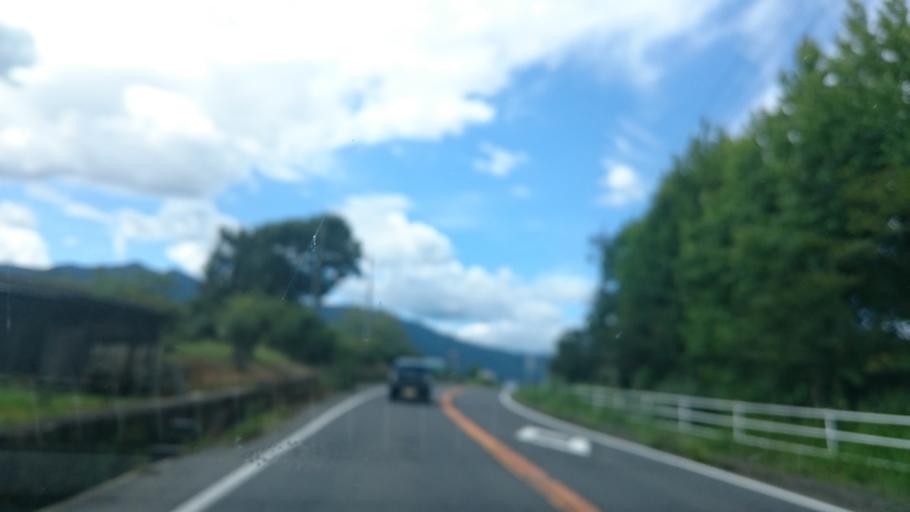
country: JP
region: Gifu
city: Nakatsugawa
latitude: 35.5450
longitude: 137.4475
